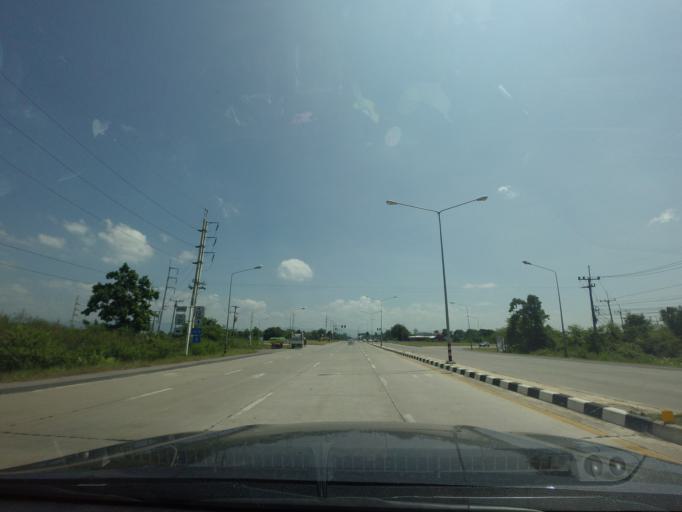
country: TH
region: Phetchabun
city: Lom Sak
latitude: 16.7658
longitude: 101.1845
